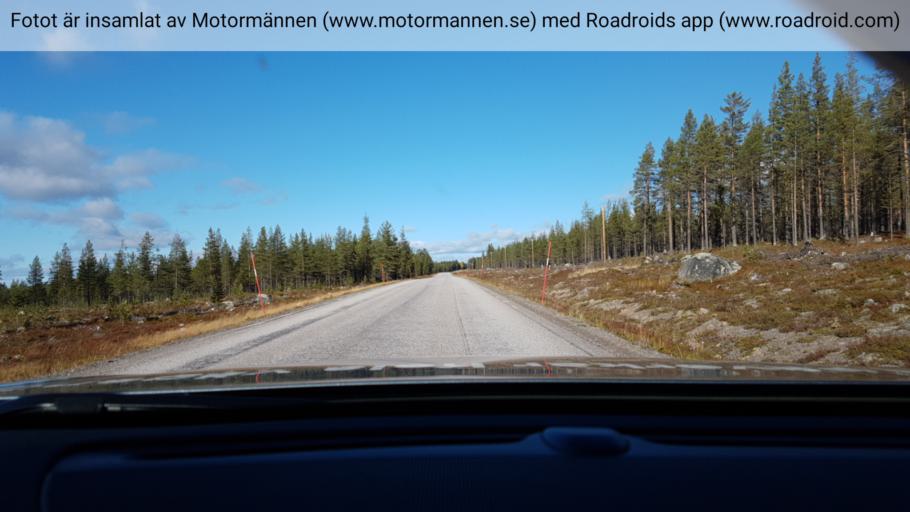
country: SE
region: Vaesterbotten
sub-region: Mala Kommun
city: Mala
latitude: 65.7781
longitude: 18.5105
